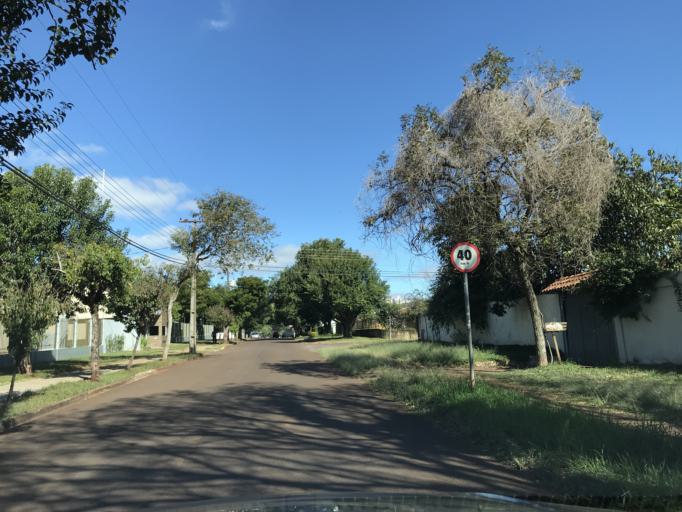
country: BR
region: Parana
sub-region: Cascavel
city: Cascavel
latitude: -24.9396
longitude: -53.4683
